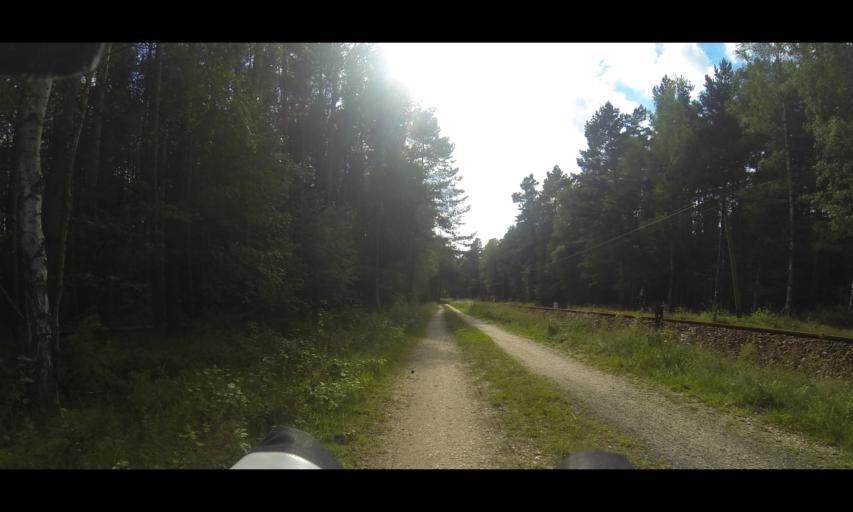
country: DE
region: Saxony
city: Laussnitz
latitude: 51.2331
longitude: 13.8608
